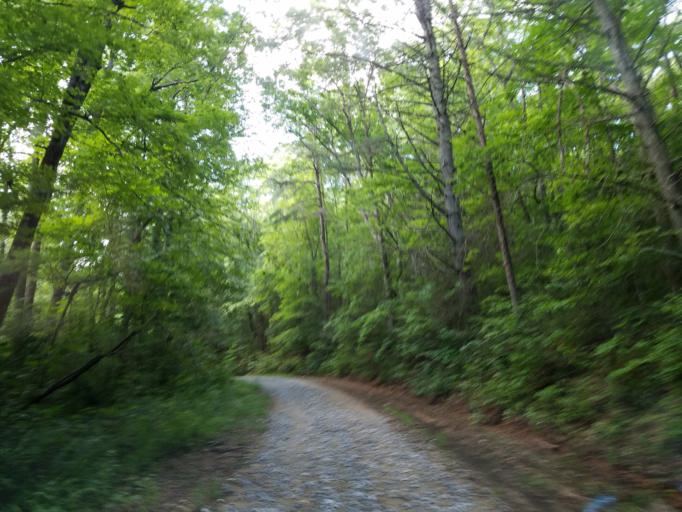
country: US
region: Georgia
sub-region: Lumpkin County
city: Dahlonega
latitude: 34.6776
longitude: -84.0414
